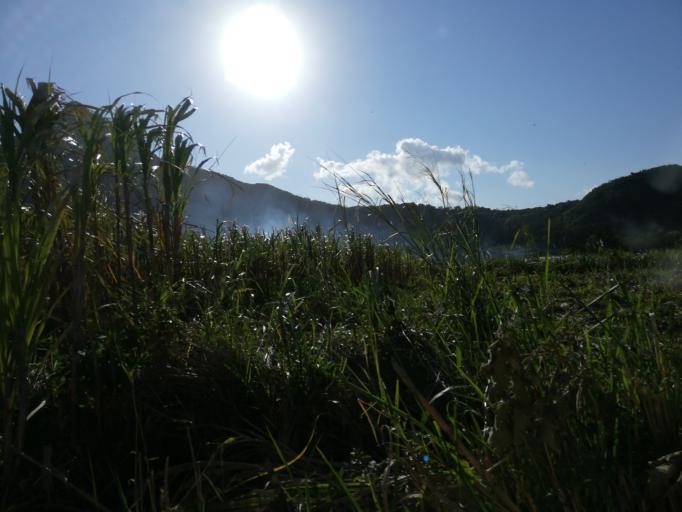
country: MU
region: Moka
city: Saint Pierre
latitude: -20.2102
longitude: 57.5253
